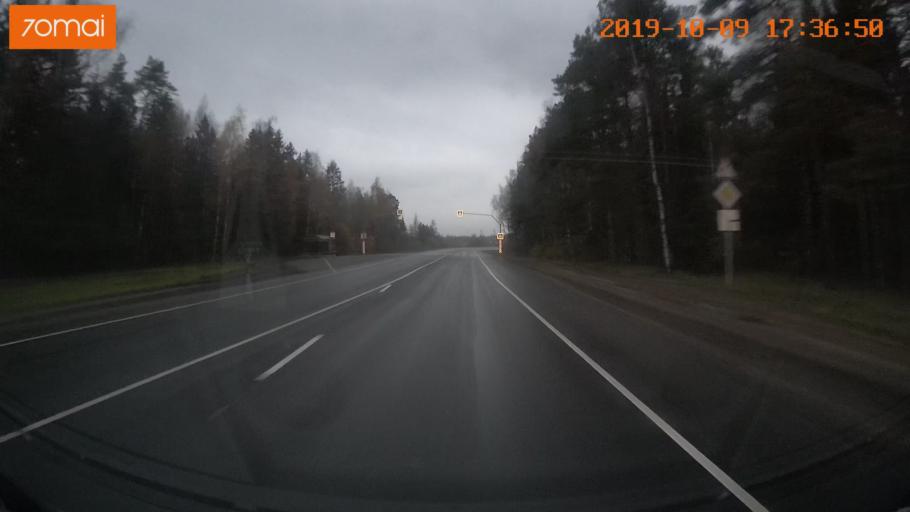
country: RU
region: Ivanovo
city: Bogorodskoye
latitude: 57.0730
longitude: 40.9920
